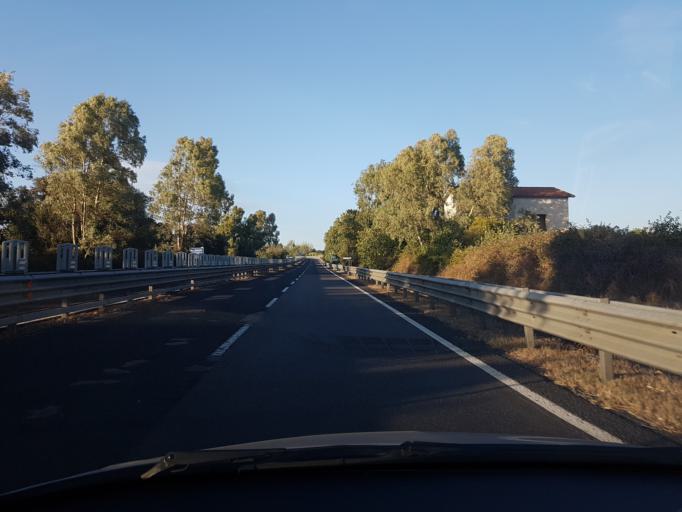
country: IT
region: Sardinia
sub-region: Provincia di Oristano
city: Paulilatino
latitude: 40.1051
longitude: 8.7889
